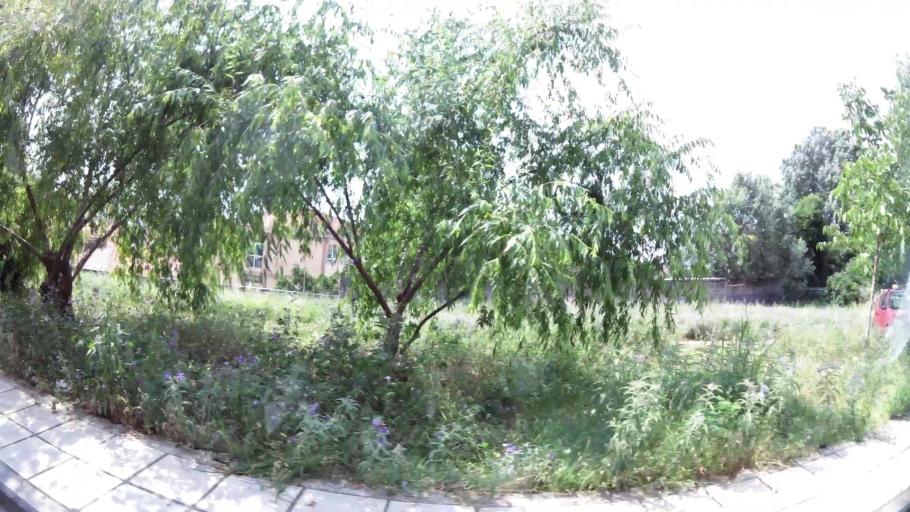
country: GR
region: Central Macedonia
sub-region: Nomos Thessalonikis
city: Polichni
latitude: 40.6653
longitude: 22.9431
